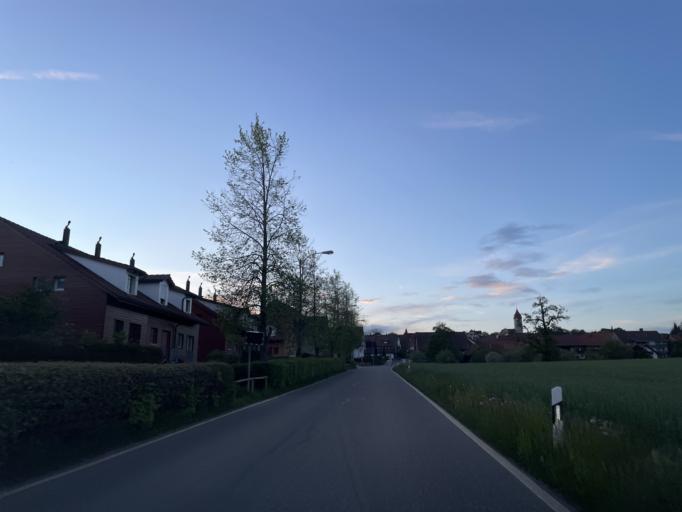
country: CH
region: Zurich
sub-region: Bezirk Winterthur
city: Brutten
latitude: 47.4693
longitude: 8.6746
